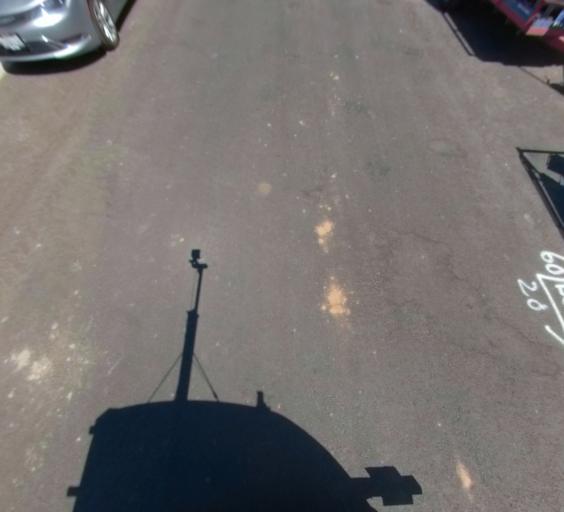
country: US
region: California
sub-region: Madera County
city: Bonadelle Ranchos-Madera Ranchos
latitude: 36.9159
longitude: -119.7990
